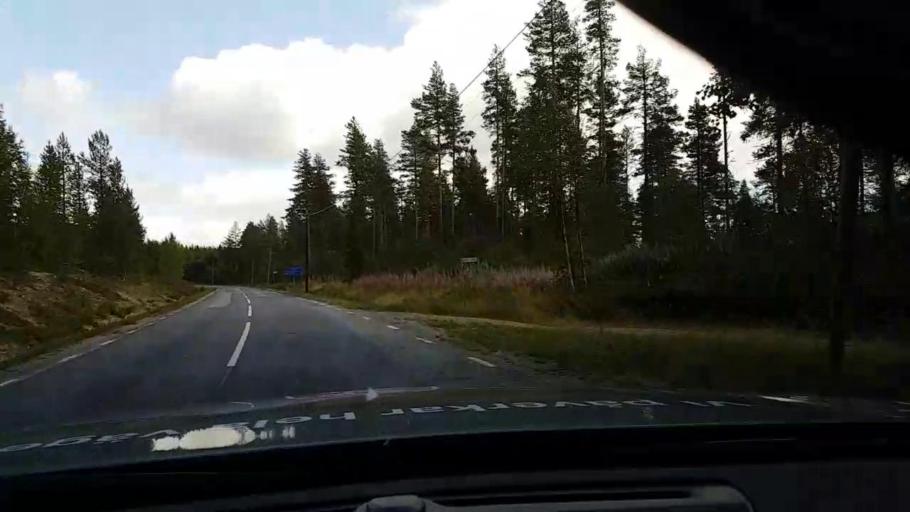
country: SE
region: Vaesterbotten
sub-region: Asele Kommun
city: Asele
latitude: 63.7946
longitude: 17.5681
